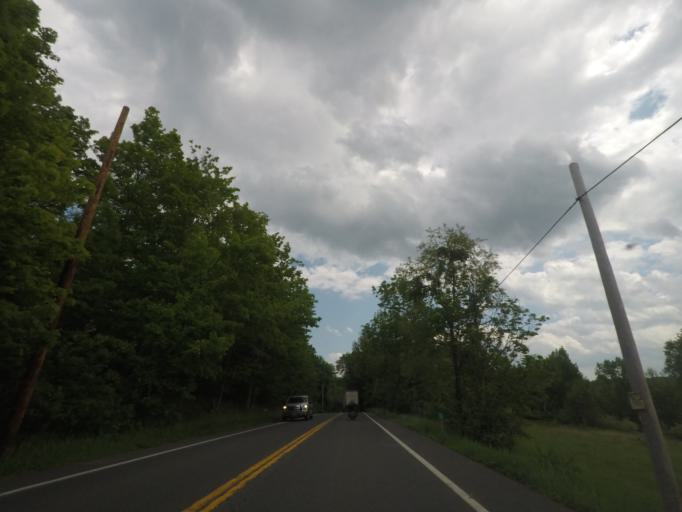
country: US
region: New York
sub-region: Dutchess County
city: Pine Plains
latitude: 42.0727
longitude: -73.6701
